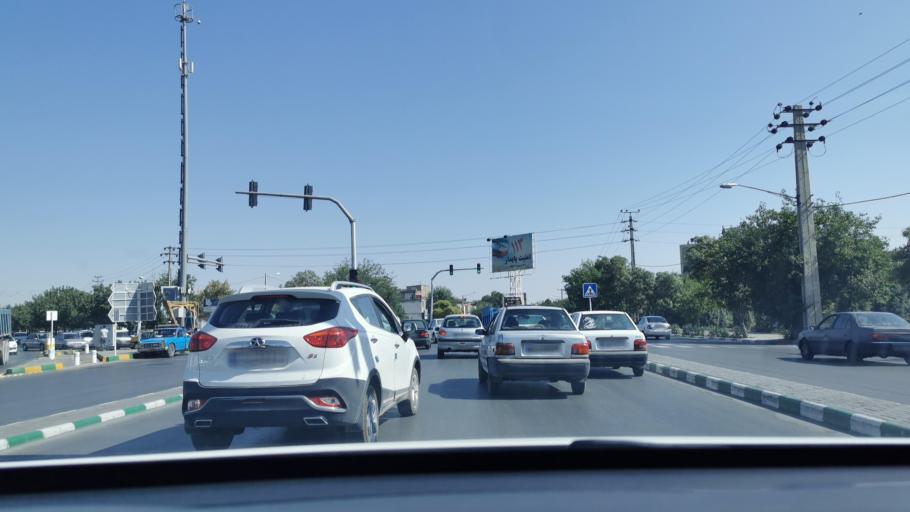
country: IR
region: Razavi Khorasan
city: Mashhad
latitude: 36.3373
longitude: 59.6261
